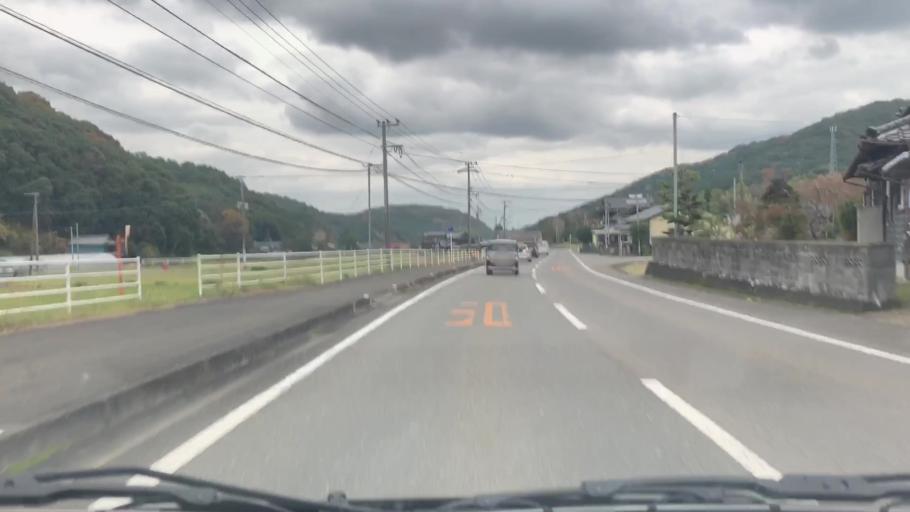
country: JP
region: Saga Prefecture
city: Kashima
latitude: 33.0987
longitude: 130.0513
